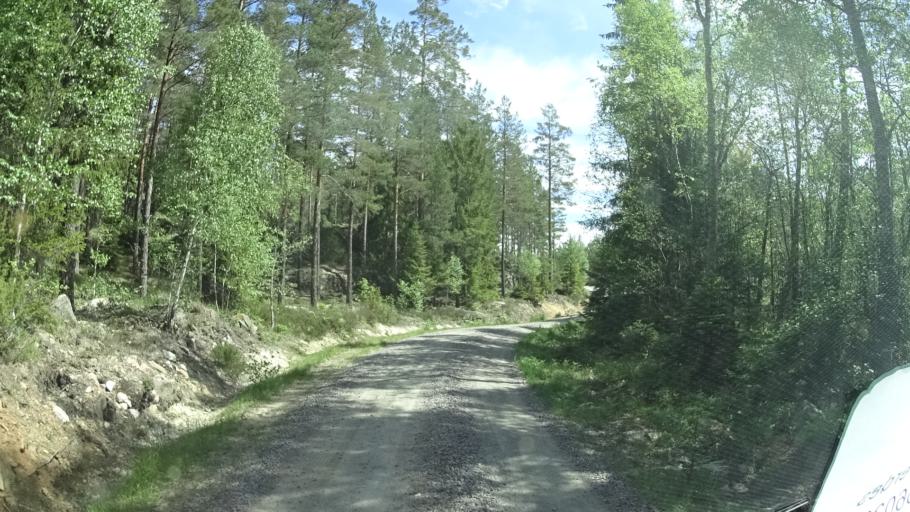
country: SE
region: OEstergoetland
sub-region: Finspangs Kommun
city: Finspang
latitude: 58.7846
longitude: 15.9029
